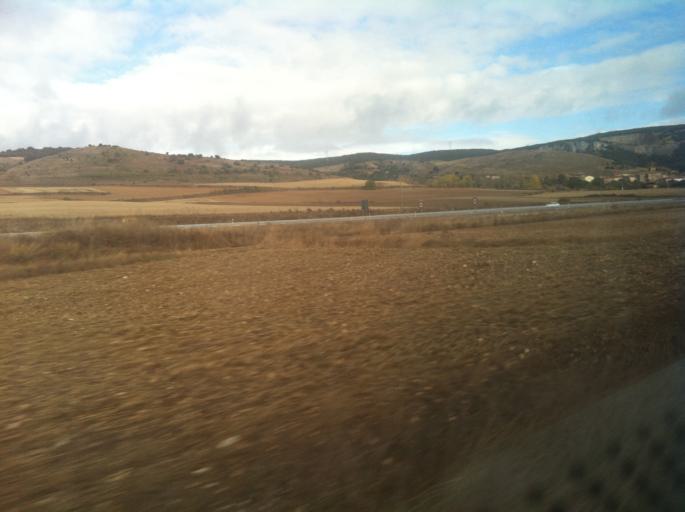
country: ES
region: Castille and Leon
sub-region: Provincia de Burgos
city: Santa Olalla de Bureba
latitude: 42.4703
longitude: -3.4443
